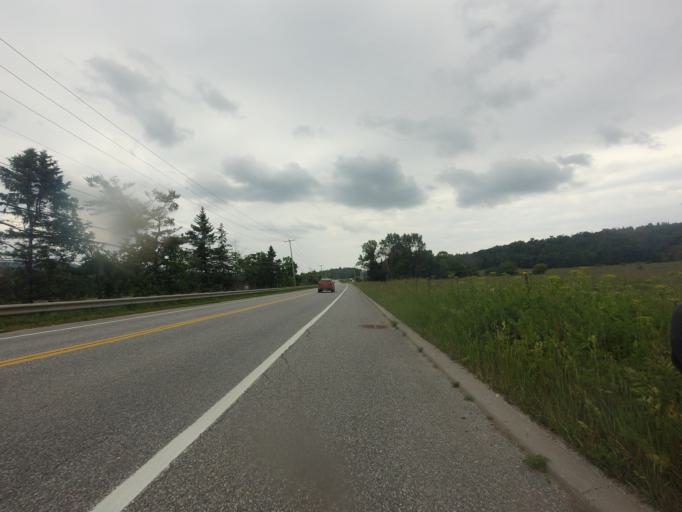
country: CA
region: Quebec
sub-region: Outaouais
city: Wakefield
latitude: 45.7368
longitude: -75.9081
